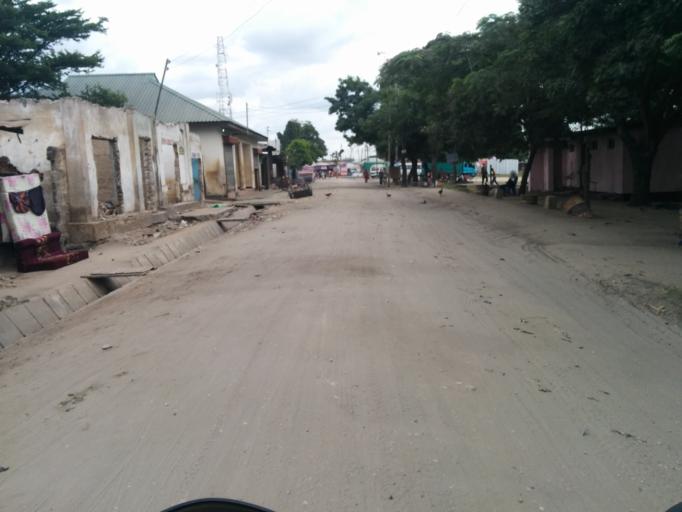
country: TZ
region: Dar es Salaam
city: Dar es Salaam
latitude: -6.8603
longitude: 39.2568
